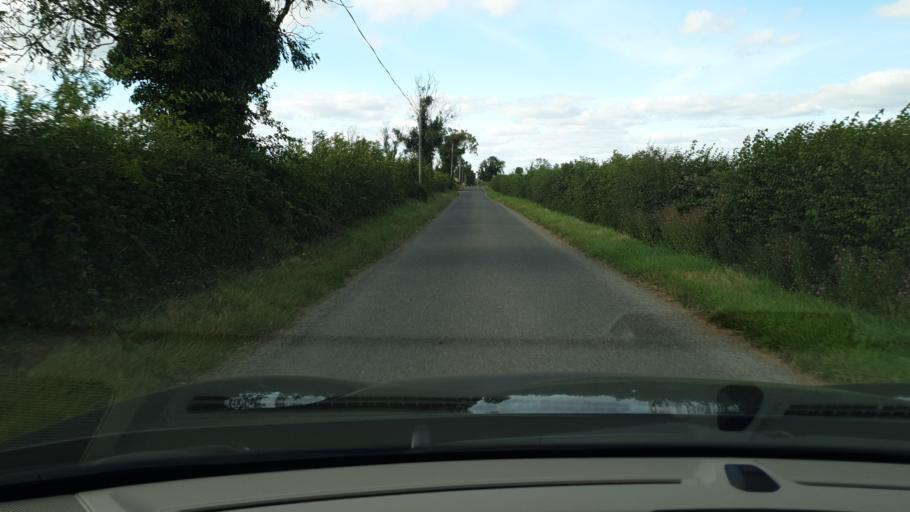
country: IE
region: Leinster
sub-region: An Mhi
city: Ashbourne
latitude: 53.4717
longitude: -6.4141
